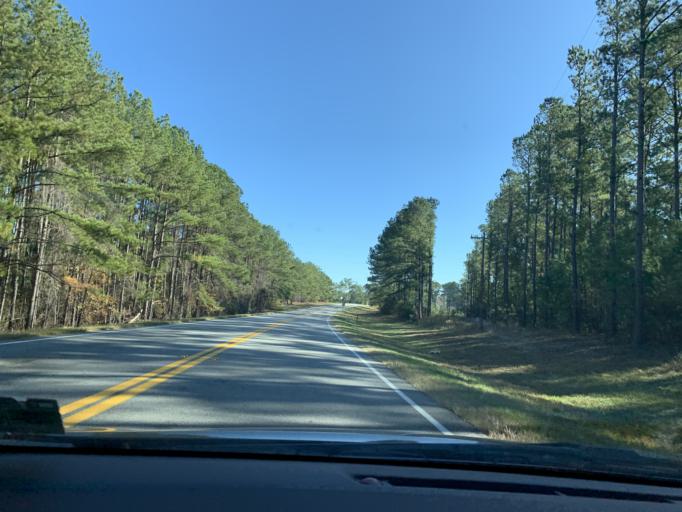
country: US
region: Georgia
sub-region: Ben Hill County
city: Fitzgerald
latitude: 31.7782
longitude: -83.0840
